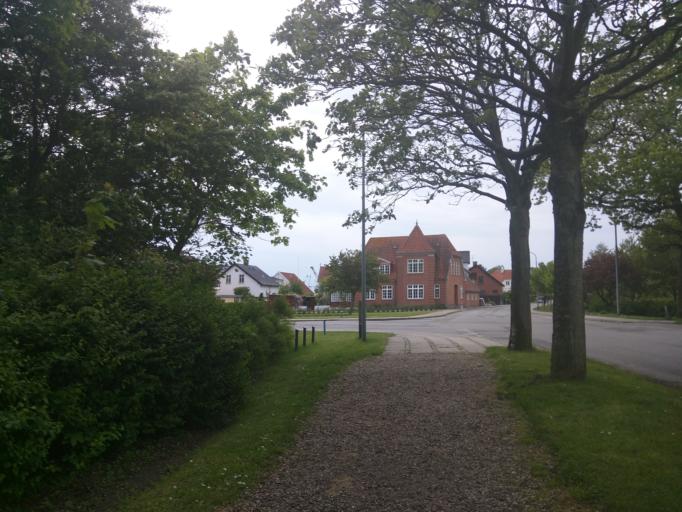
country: DK
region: North Denmark
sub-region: Morso Kommune
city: Nykobing Mors
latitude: 56.7957
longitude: 8.8724
